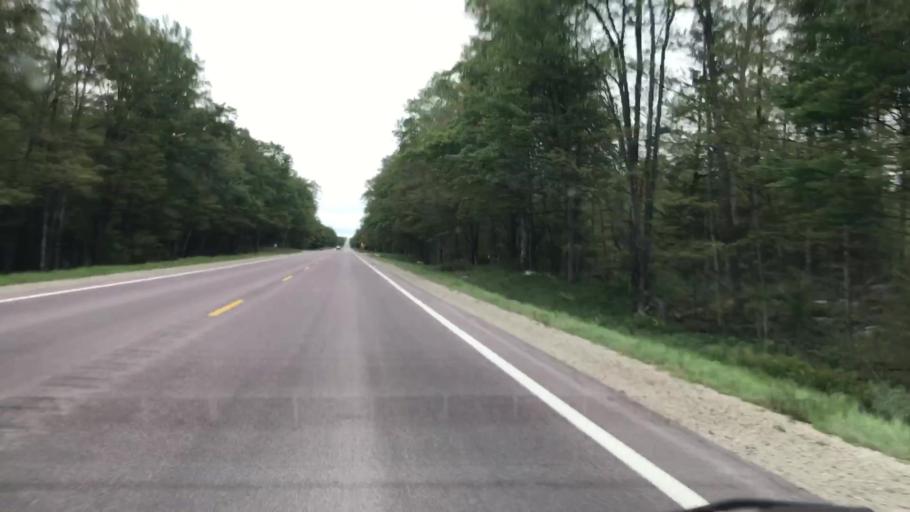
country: US
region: Michigan
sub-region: Luce County
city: Newberry
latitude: 46.2486
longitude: -85.5724
